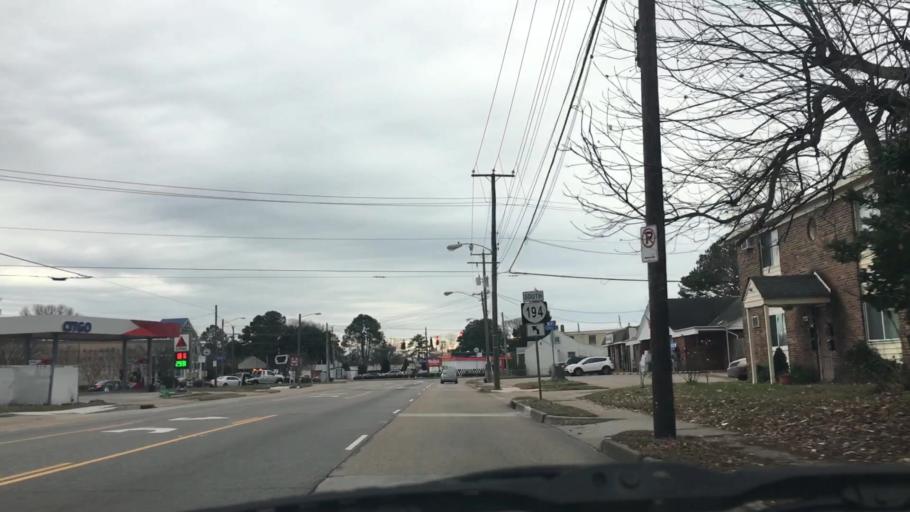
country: US
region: Virginia
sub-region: City of Norfolk
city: Norfolk
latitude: 36.8722
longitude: -76.2323
